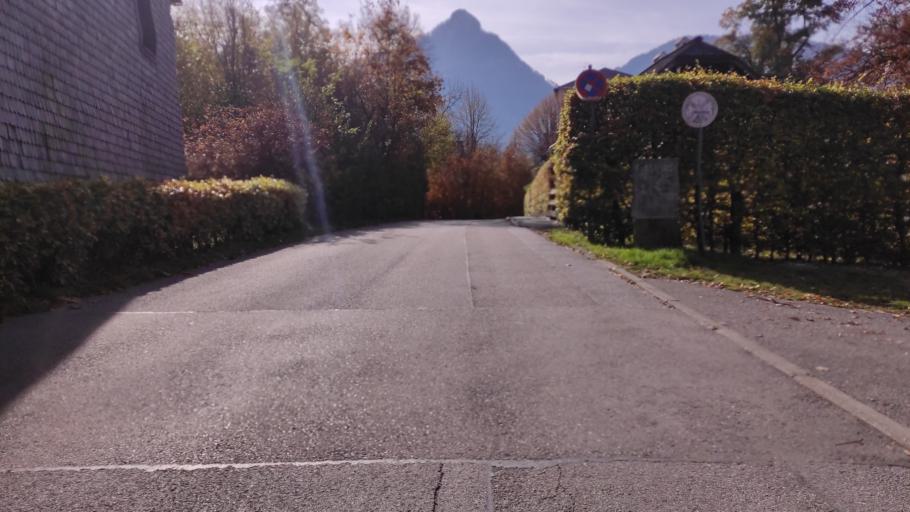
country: AT
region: Salzburg
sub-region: Politischer Bezirk Salzburg-Umgebung
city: Strobl
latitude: 47.7212
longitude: 13.4856
